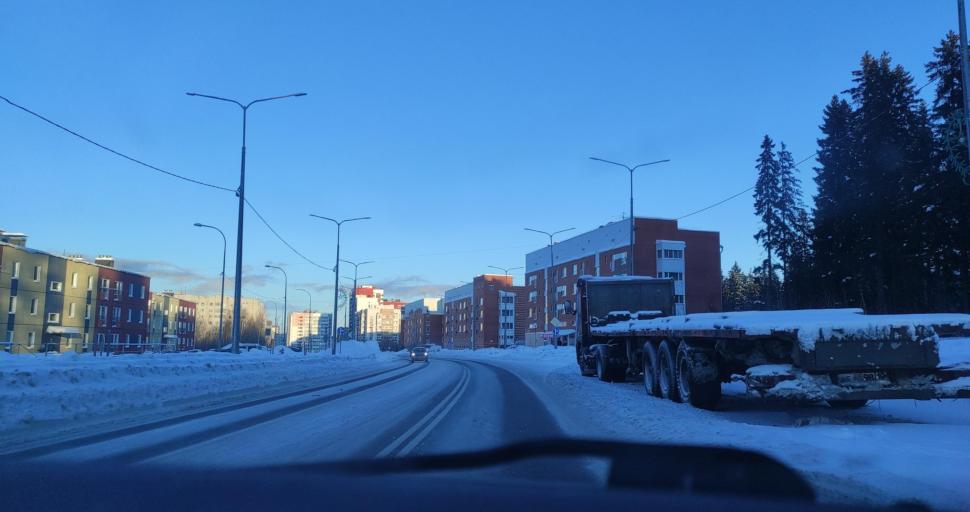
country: RU
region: Republic of Karelia
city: Petrozavodsk
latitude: 61.7760
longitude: 34.3220
